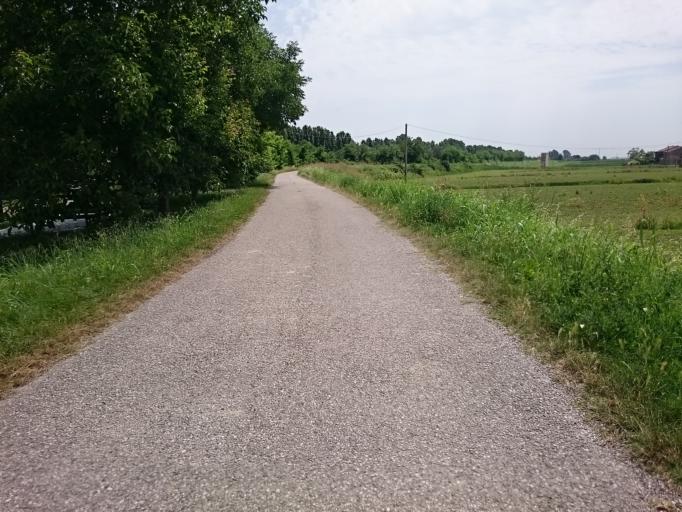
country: IT
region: Veneto
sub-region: Provincia di Venezia
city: Valli
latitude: 45.2270
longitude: 12.1444
